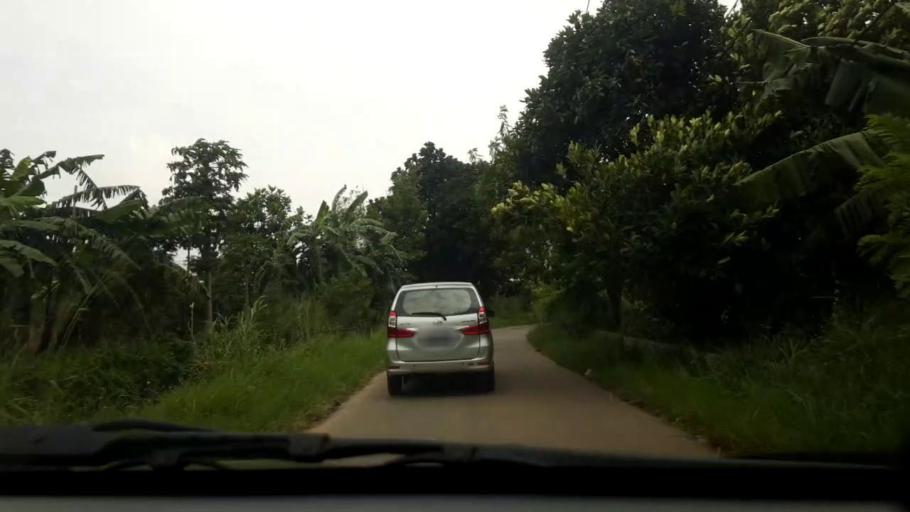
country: ID
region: West Java
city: Cileunyi
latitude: -6.9470
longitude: 107.7132
